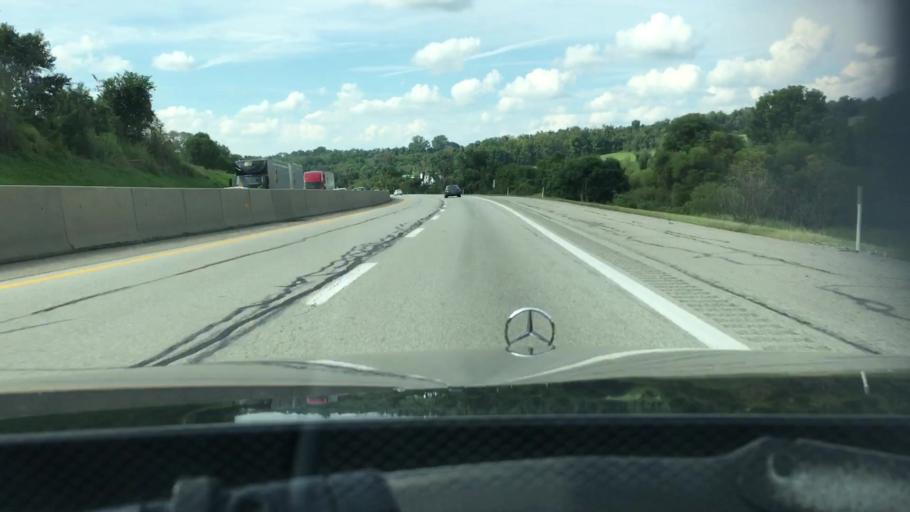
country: US
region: Pennsylvania
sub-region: Westmoreland County
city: Mount Pleasant
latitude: 40.1877
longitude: -79.5330
